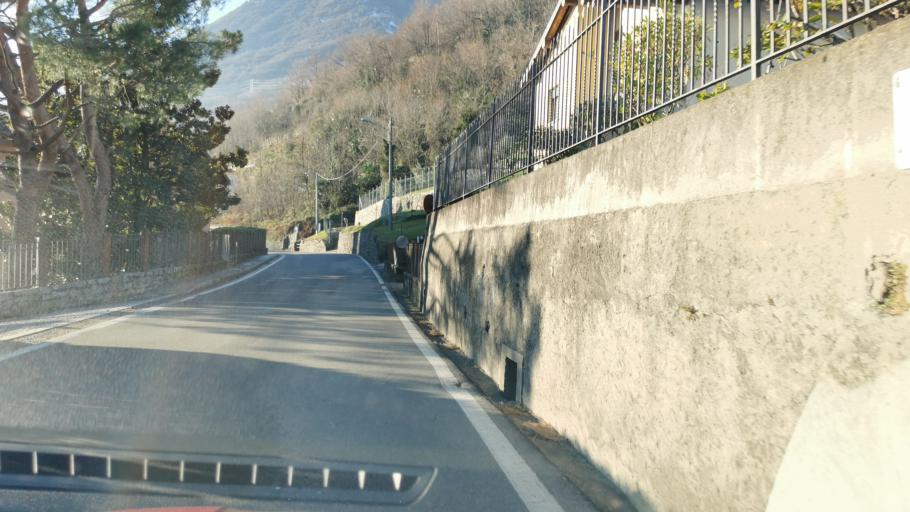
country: IT
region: Lombardy
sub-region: Provincia di Como
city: Gera Lario
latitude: 46.1699
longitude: 9.3633
